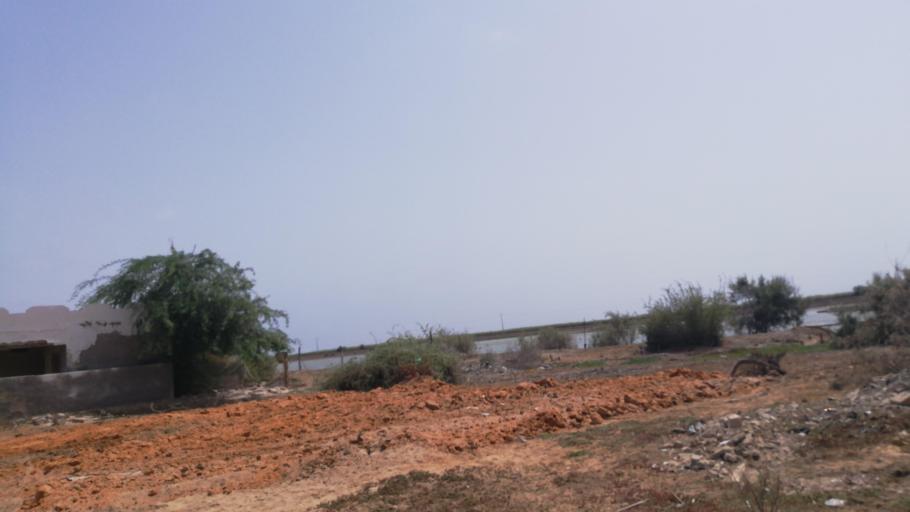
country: SN
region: Saint-Louis
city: Saint-Louis
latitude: 16.3595
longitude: -16.2745
